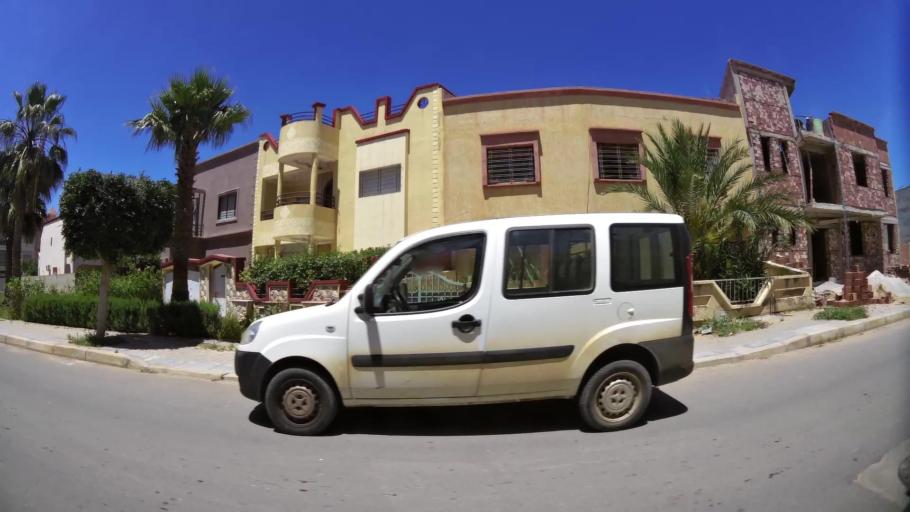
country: MA
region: Oriental
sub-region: Berkane-Taourirt
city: Madagh
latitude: 35.0819
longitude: -2.2265
